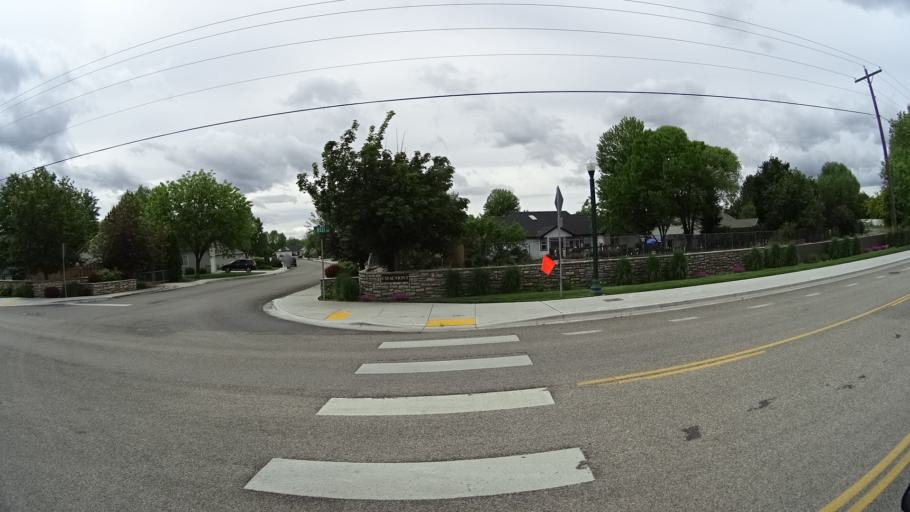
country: US
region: Idaho
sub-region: Ada County
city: Eagle
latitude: 43.6945
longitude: -116.3243
